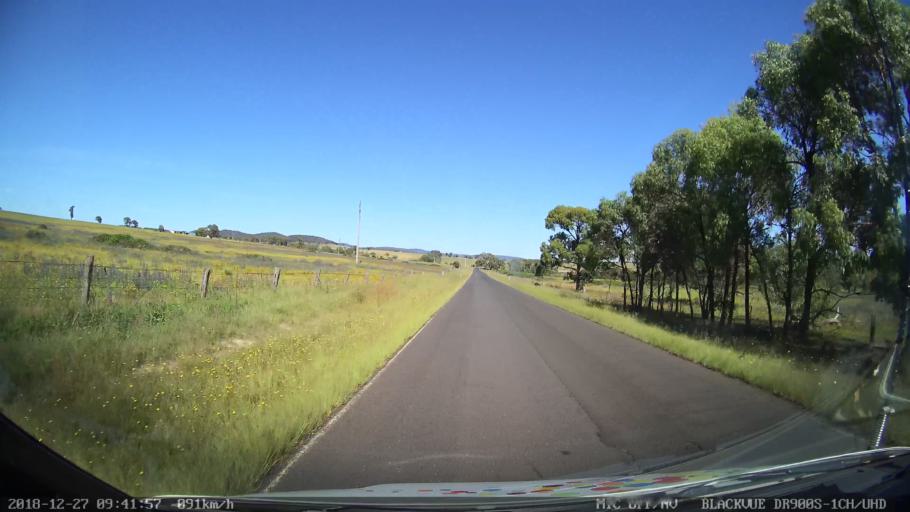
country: AU
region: New South Wales
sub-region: Lithgow
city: Portland
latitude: -33.3005
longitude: 150.0147
